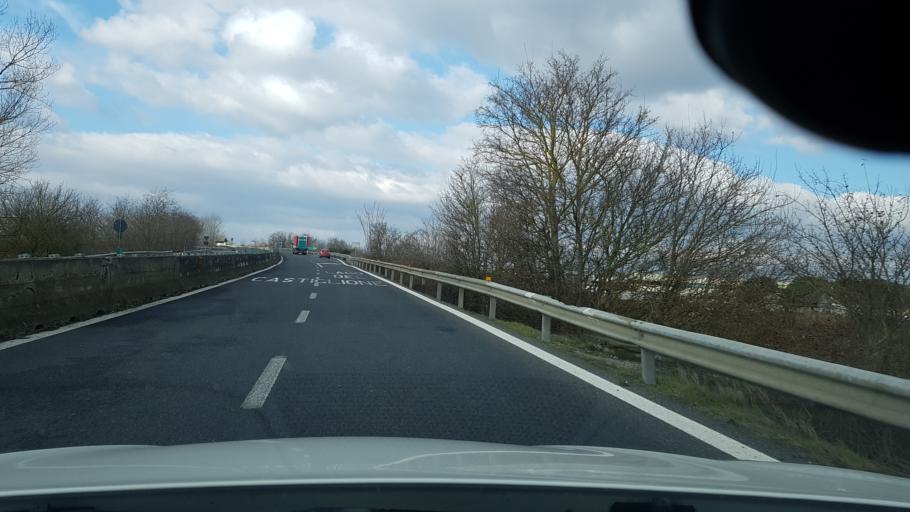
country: IT
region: Tuscany
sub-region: Province of Arezzo
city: Terontola
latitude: 43.1896
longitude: 12.0183
